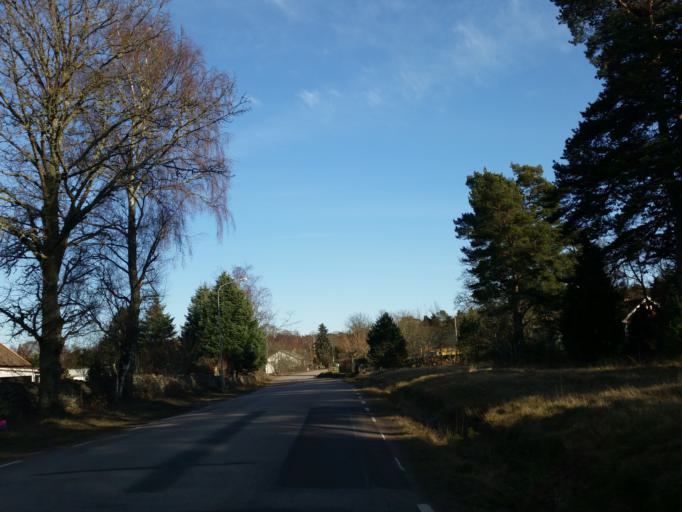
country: SE
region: Kalmar
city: Faerjestaden
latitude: 56.7829
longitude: 16.4433
